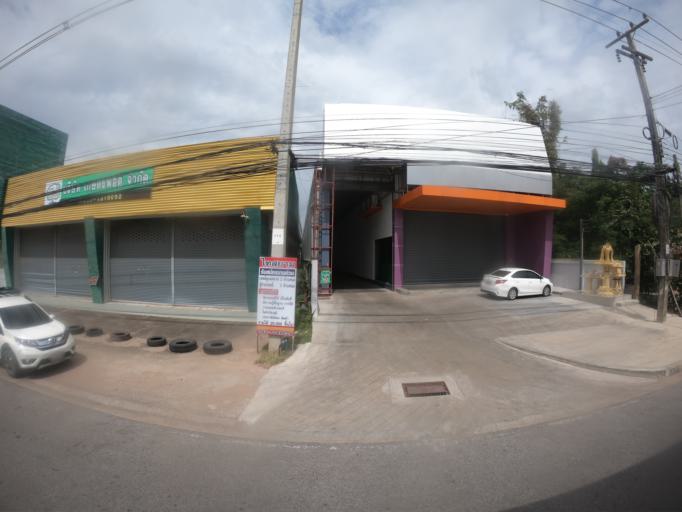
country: TH
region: Roi Et
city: Roi Et
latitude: 16.0594
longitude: 103.6301
